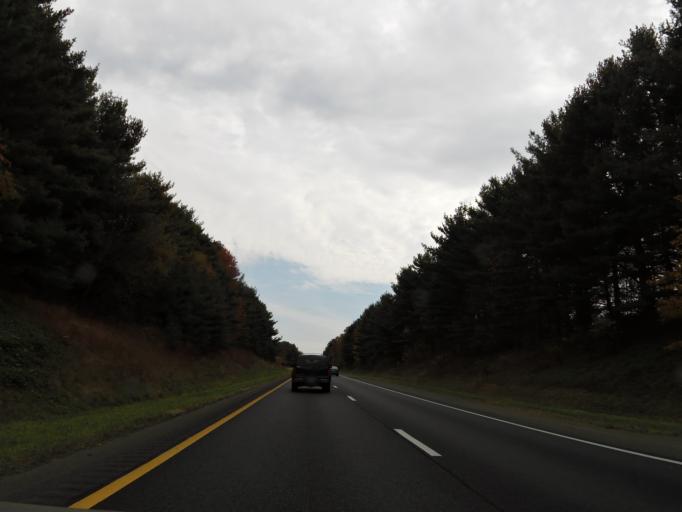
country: US
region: Virginia
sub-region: Carroll County
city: Woodlawn
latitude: 36.7743
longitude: -80.8145
